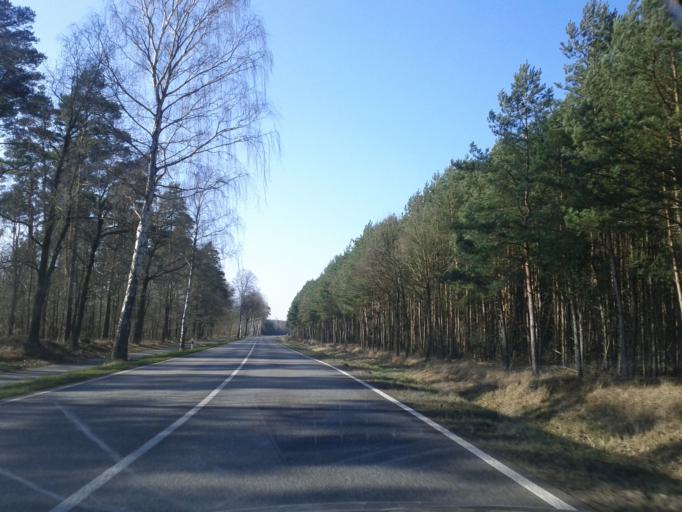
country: DE
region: Brandenburg
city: Spreenhagen
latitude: 52.4035
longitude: 13.8852
